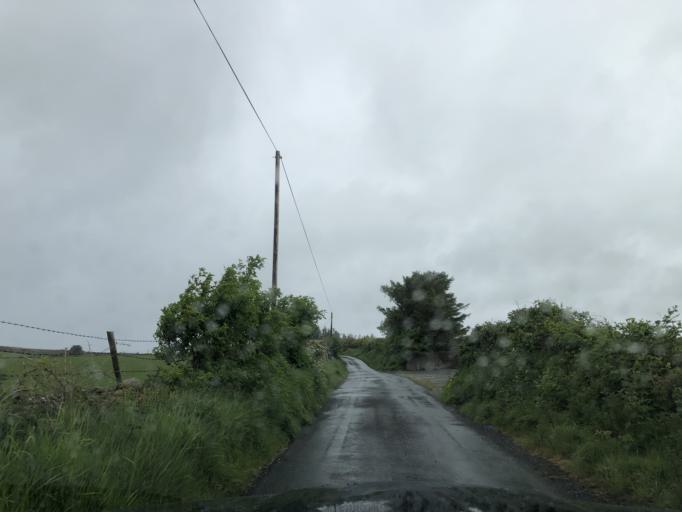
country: GB
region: Northern Ireland
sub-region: Moyle District
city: Ballycastle
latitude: 55.2019
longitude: -6.1728
